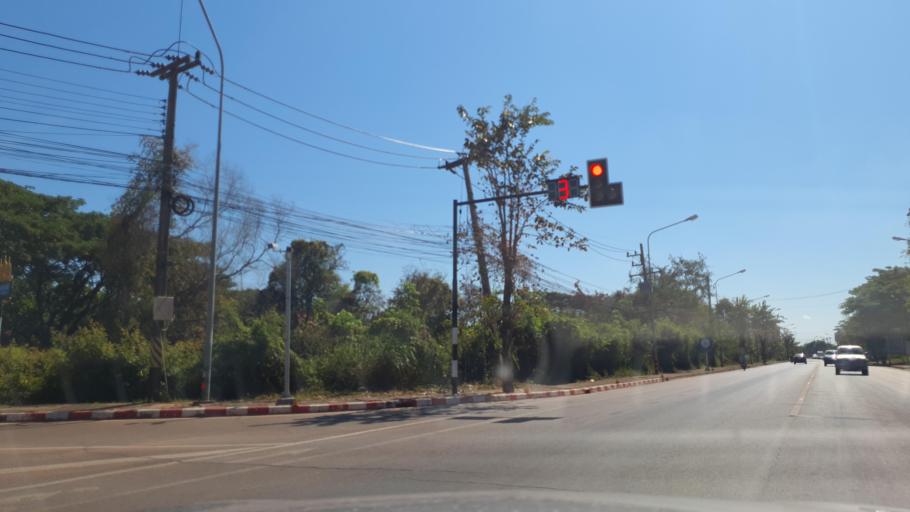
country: TH
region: Sakon Nakhon
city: Sakon Nakhon
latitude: 17.1570
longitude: 104.1262
